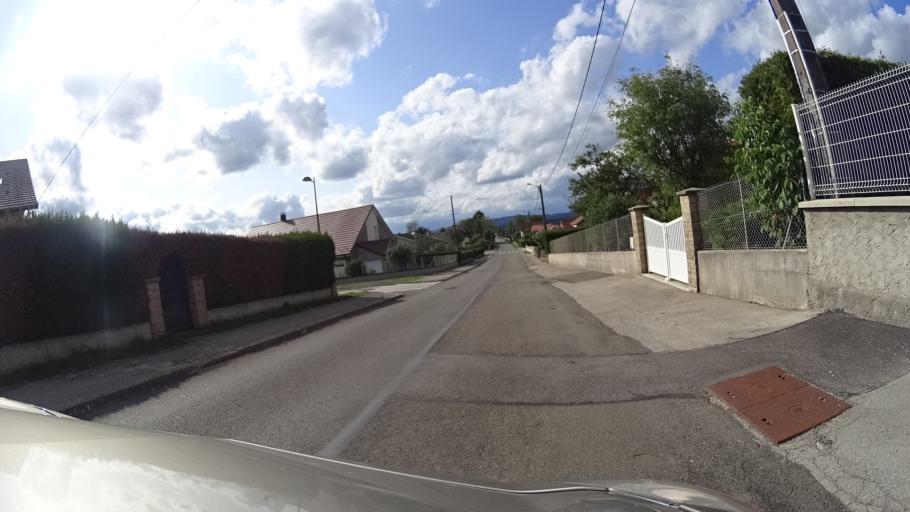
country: FR
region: Franche-Comte
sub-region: Departement du Doubs
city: Mamirolle
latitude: 47.2009
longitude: 6.1587
